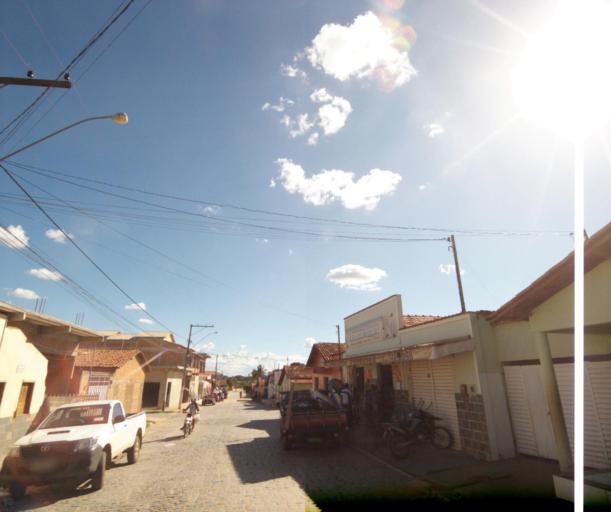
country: BR
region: Bahia
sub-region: Carinhanha
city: Carinhanha
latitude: -14.1824
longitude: -44.5413
